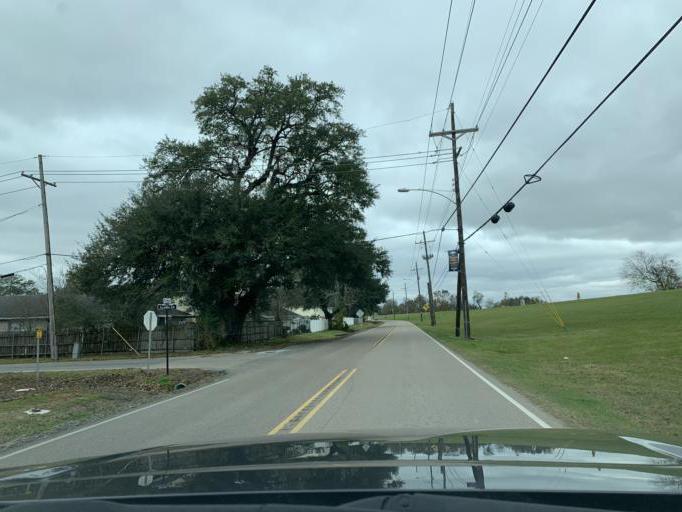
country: US
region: Louisiana
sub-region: Jefferson Parish
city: River Ridge
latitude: 29.9567
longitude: -90.2362
